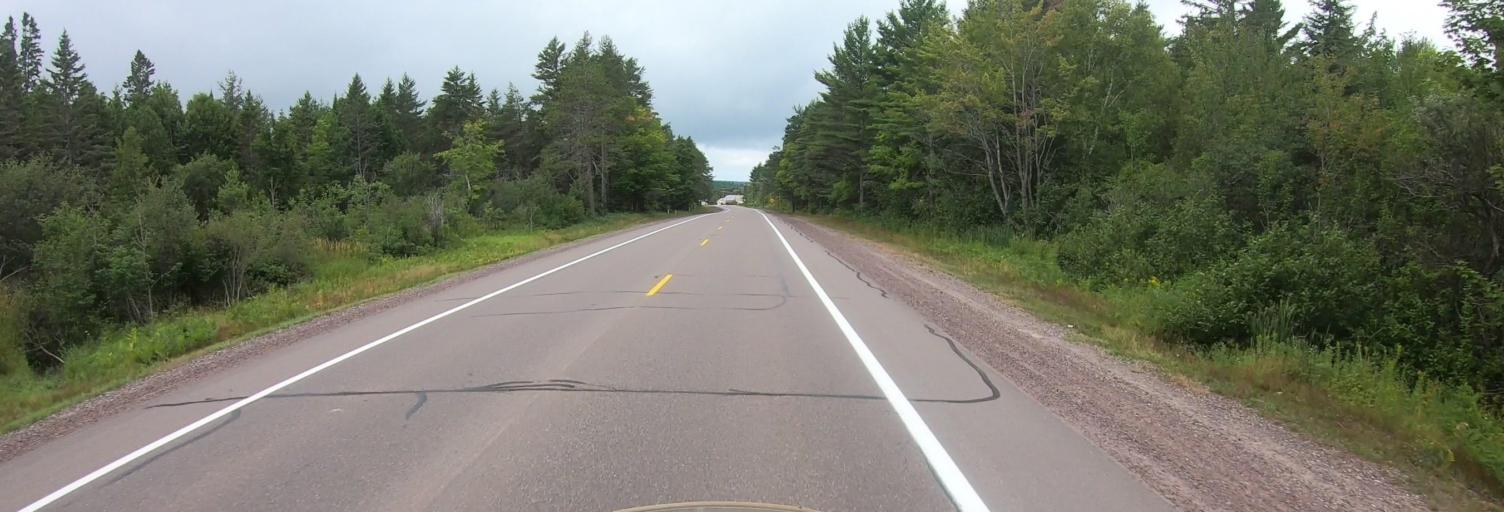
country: US
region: Michigan
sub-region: Houghton County
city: Laurium
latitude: 47.3003
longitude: -88.3827
